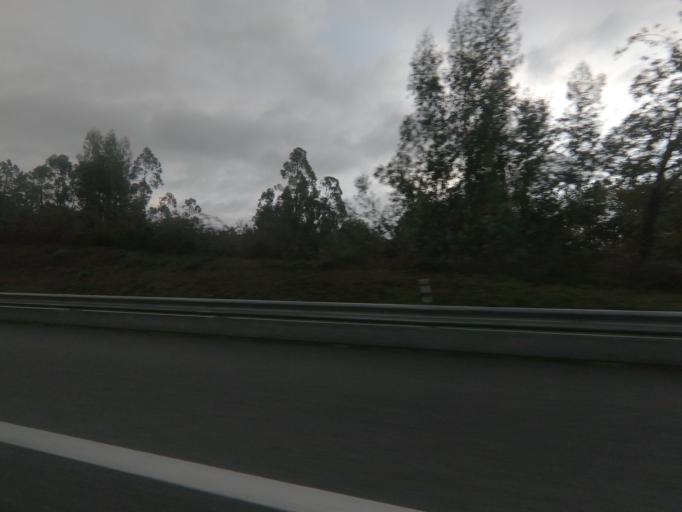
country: PT
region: Viana do Castelo
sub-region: Ponte de Lima
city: Ponte de Lima
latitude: 41.7493
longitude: -8.5567
